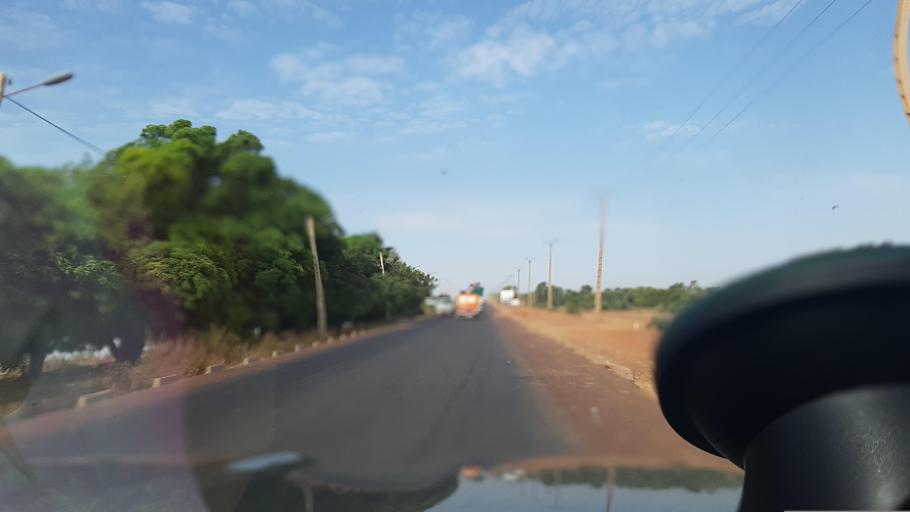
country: ML
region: Segou
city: Markala
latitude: 13.6821
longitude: -6.0871
